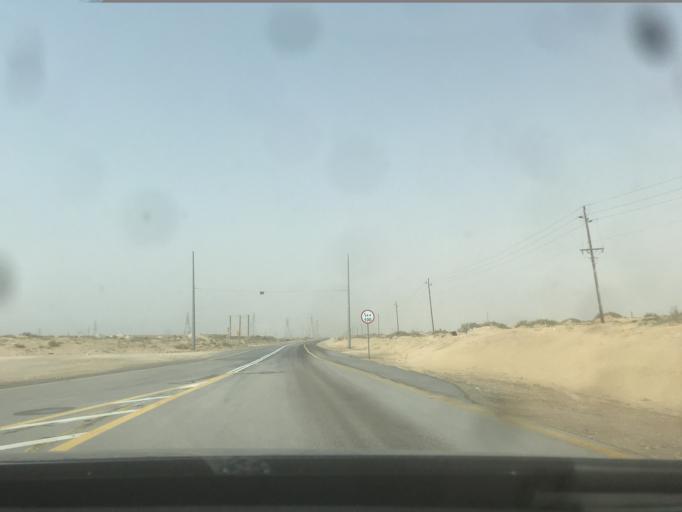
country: SA
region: Eastern Province
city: Abqaiq
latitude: 25.9345
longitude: 49.7305
